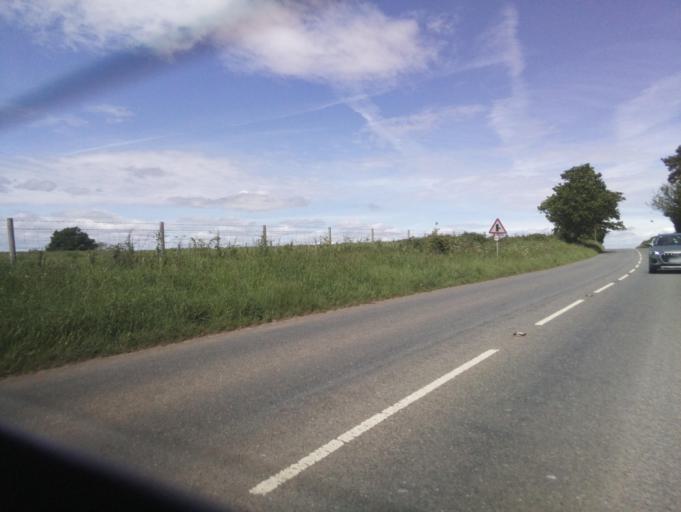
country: GB
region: England
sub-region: Devon
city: Uffculme
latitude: 50.8339
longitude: -3.3018
